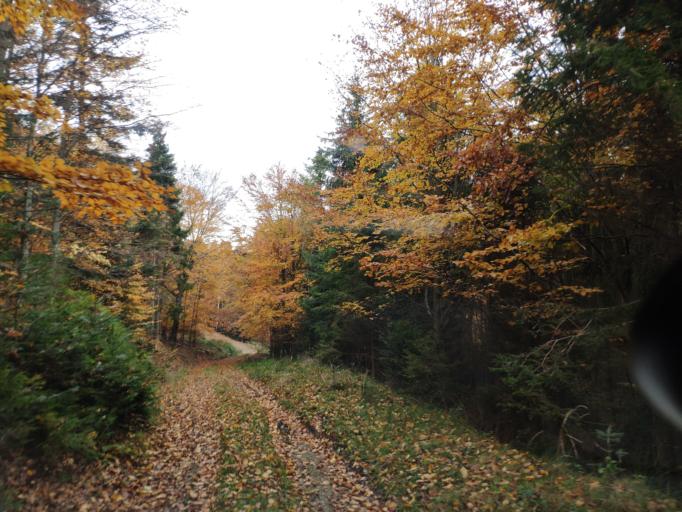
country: SK
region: Kosicky
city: Medzev
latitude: 48.7579
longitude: 20.9788
